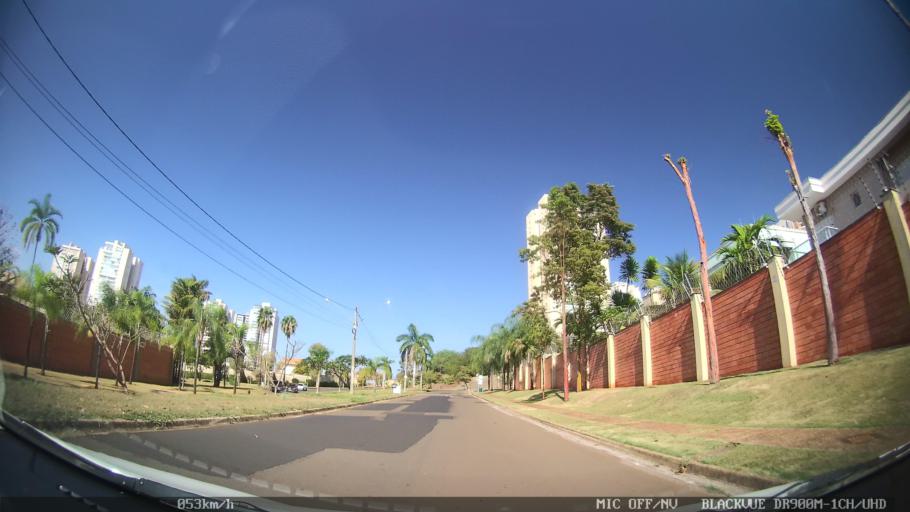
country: BR
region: Sao Paulo
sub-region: Ribeirao Preto
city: Ribeirao Preto
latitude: -21.2144
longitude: -47.8016
